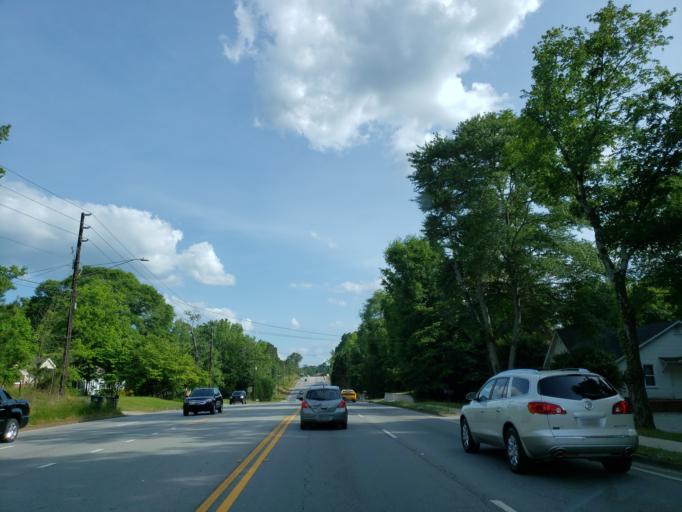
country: US
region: Georgia
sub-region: Carroll County
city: Carrollton
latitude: 33.5908
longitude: -85.0791
